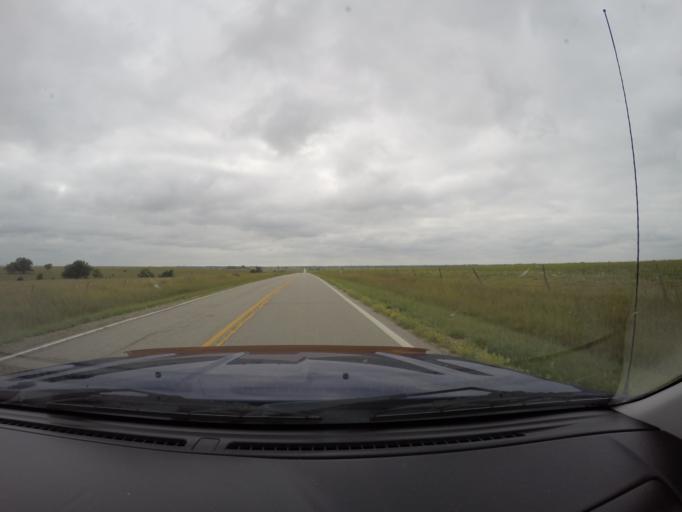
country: US
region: Kansas
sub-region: Morris County
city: Council Grove
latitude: 38.7977
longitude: -96.5975
